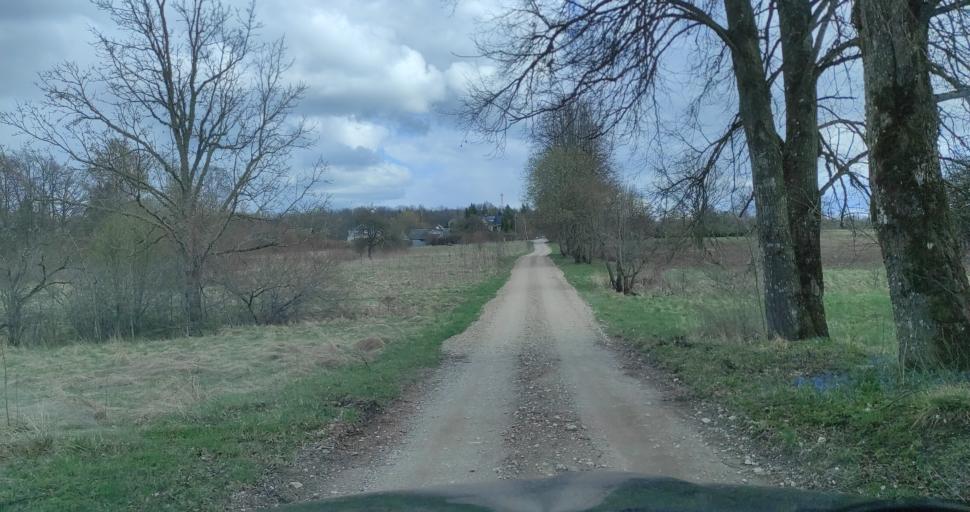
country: LV
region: Aizpute
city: Aizpute
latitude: 56.7162
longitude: 21.5872
